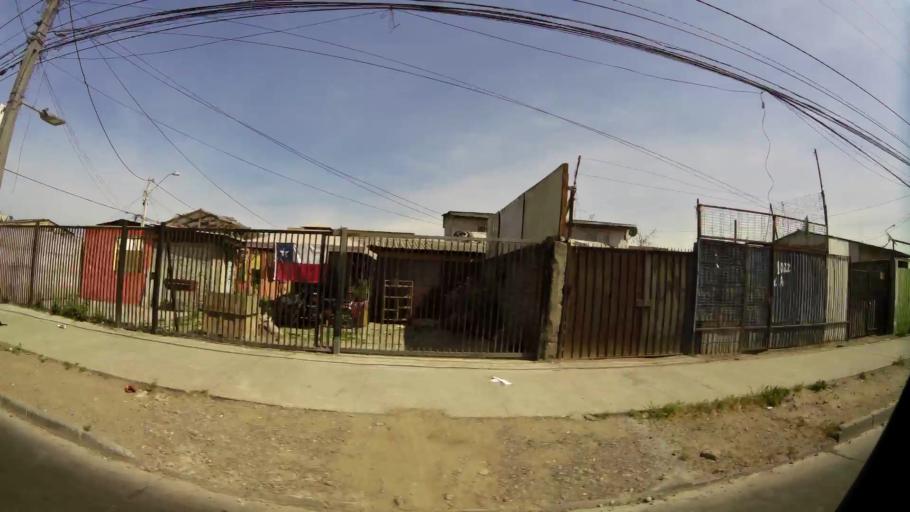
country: CL
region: Santiago Metropolitan
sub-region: Provincia de Santiago
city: Lo Prado
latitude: -33.4386
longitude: -70.7637
